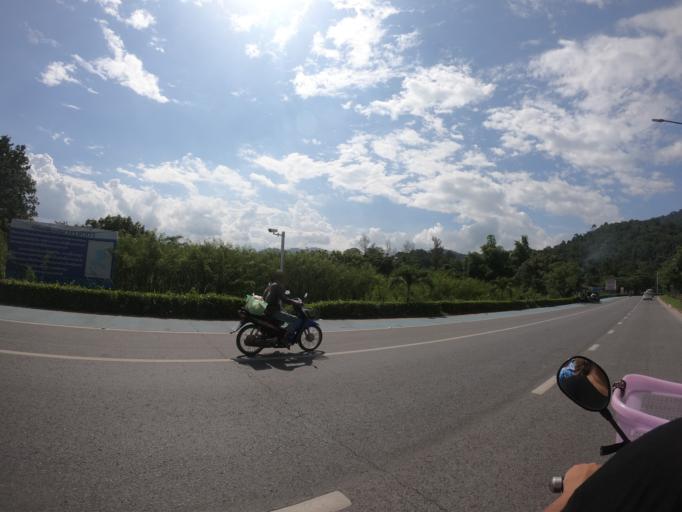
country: TH
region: Nakhon Nayok
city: Nakhon Nayok
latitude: 14.3197
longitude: 101.3113
